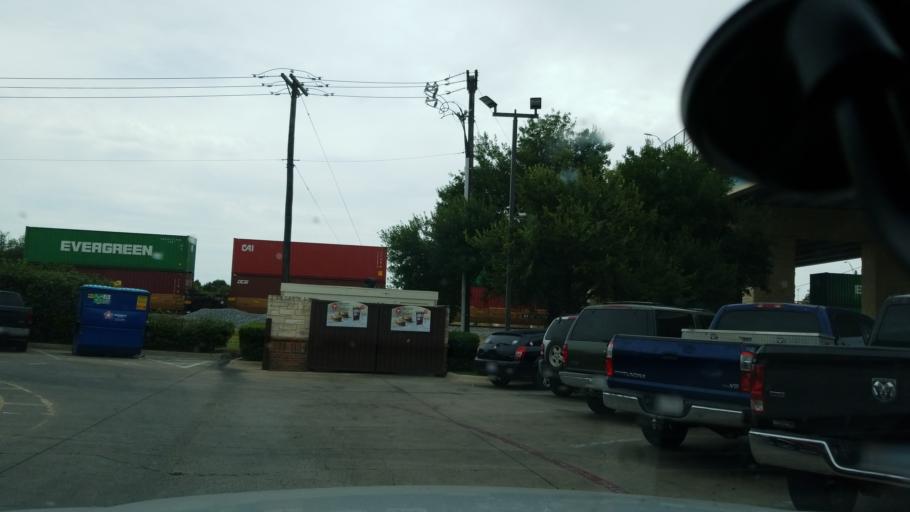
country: US
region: Texas
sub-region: Dallas County
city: Grand Prairie
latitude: 32.7457
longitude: -96.9943
